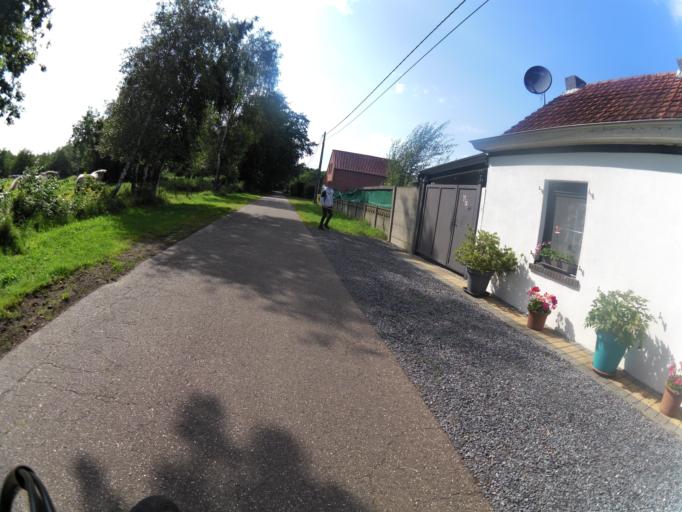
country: BE
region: Flanders
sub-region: Provincie Antwerpen
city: Balen
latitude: 51.1798
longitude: 5.1521
